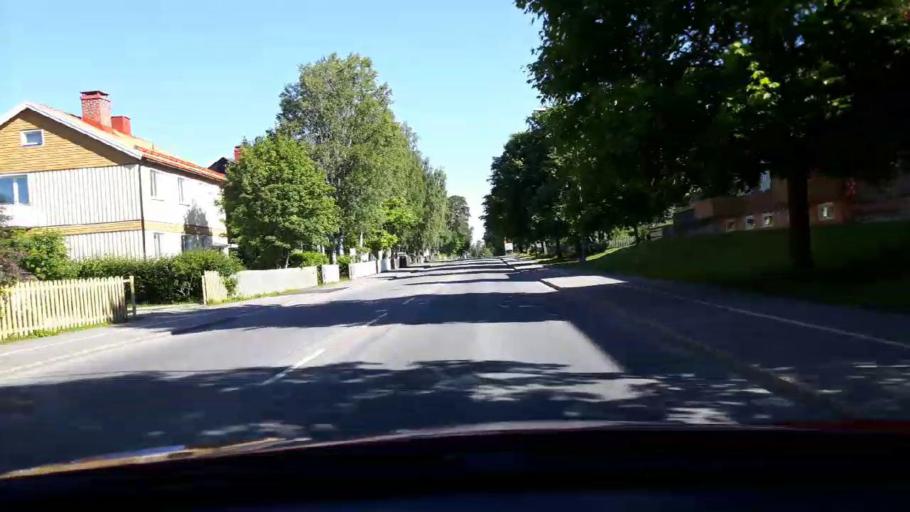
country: SE
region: Jaemtland
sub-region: OEstersunds Kommun
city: Ostersund
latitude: 63.1839
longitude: 14.6540
